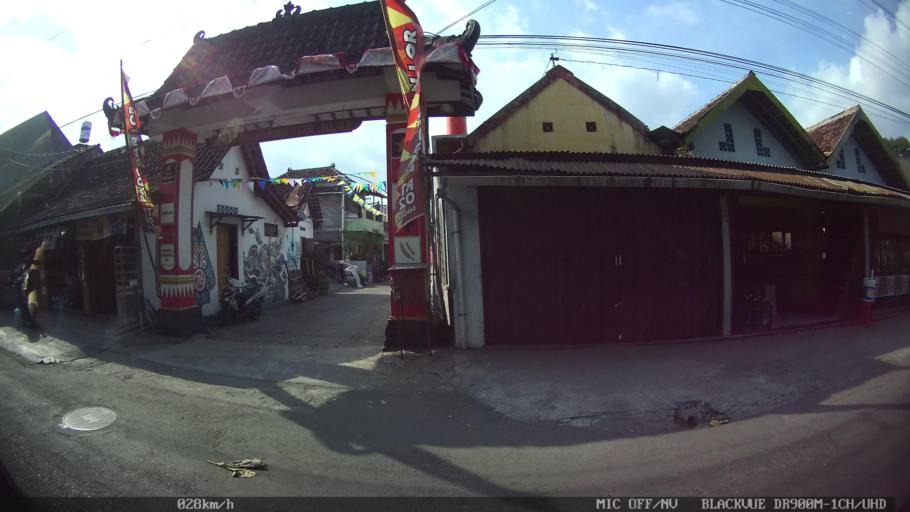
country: ID
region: Daerah Istimewa Yogyakarta
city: Kasihan
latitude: -7.8290
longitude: 110.3421
